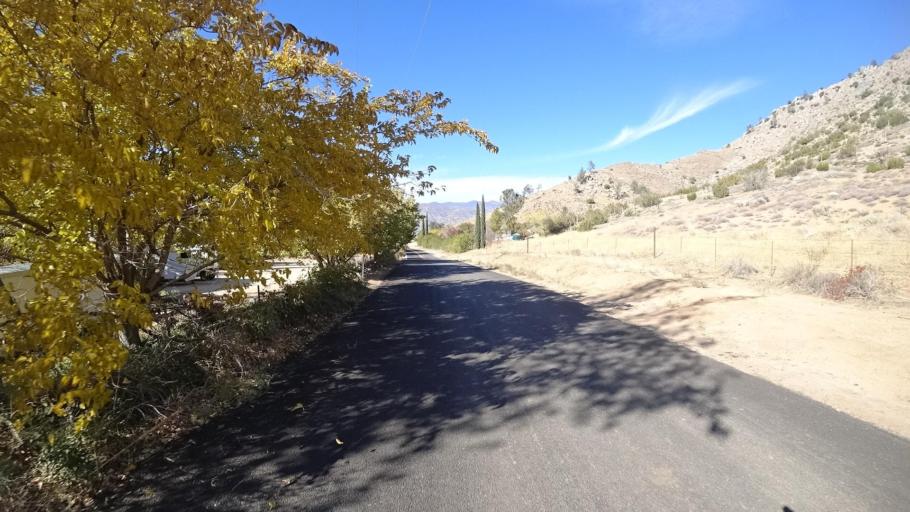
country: US
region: California
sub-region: Kern County
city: Lake Isabella
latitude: 35.5949
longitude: -118.4506
